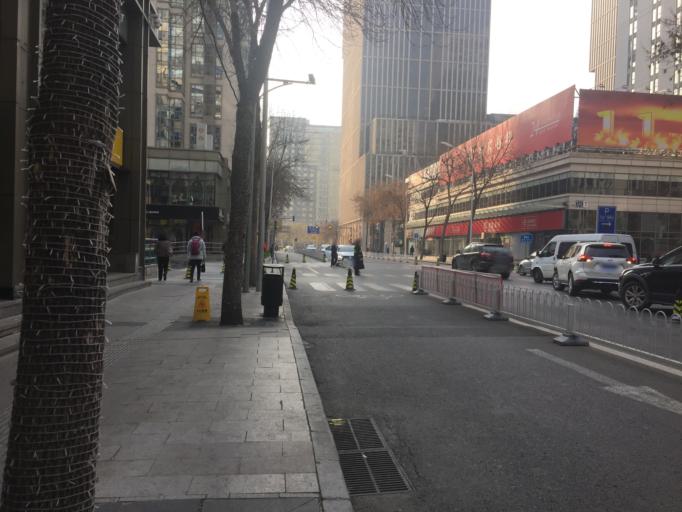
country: CN
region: Beijing
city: Chaowai
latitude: 39.9099
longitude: 116.4655
